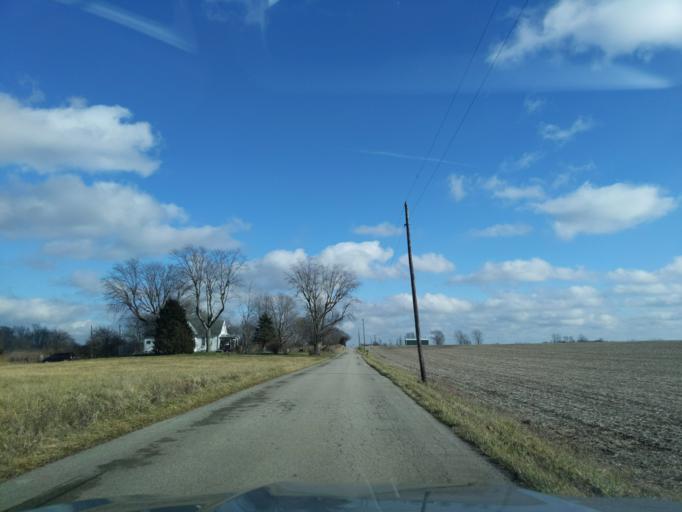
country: US
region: Indiana
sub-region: Decatur County
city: Greensburg
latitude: 39.2781
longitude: -85.4743
